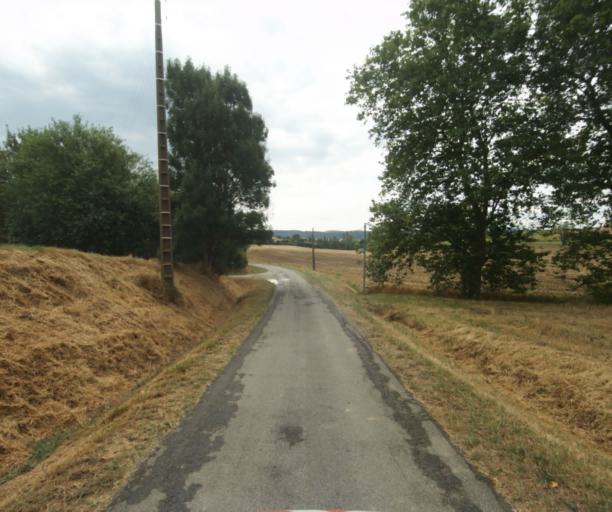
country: FR
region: Midi-Pyrenees
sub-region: Departement de la Haute-Garonne
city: Revel
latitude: 43.4385
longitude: 1.9622
